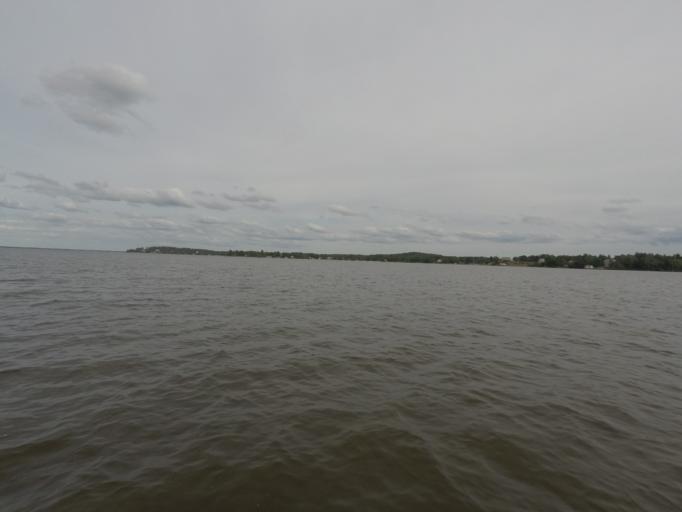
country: SE
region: Soedermanland
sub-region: Eskilstuna Kommun
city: Hallbybrunn
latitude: 59.4591
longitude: 16.4131
